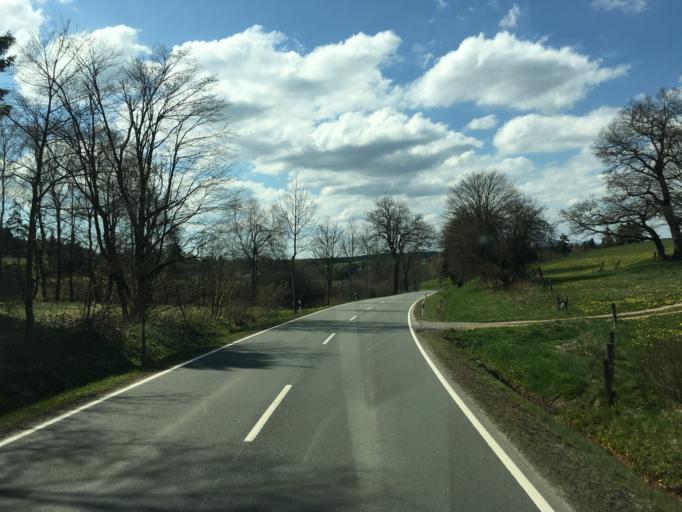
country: DE
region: Saxony-Anhalt
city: Hasselfelde
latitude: 51.6831
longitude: 10.7977
